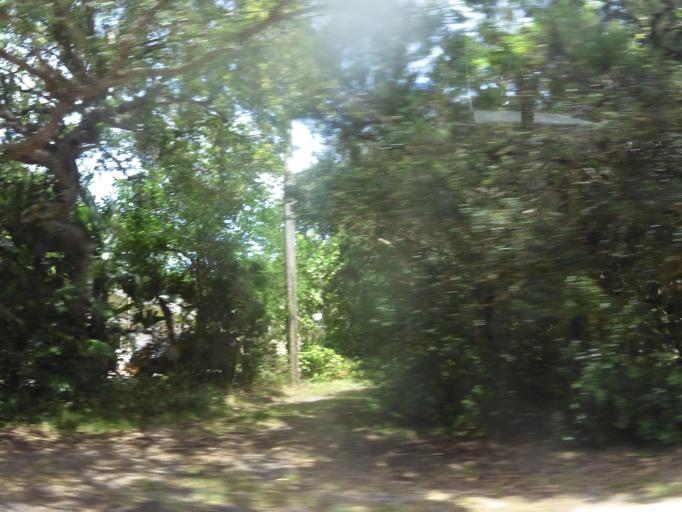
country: US
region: Florida
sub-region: Volusia County
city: Ponce Inlet
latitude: 29.0872
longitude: -80.9339
